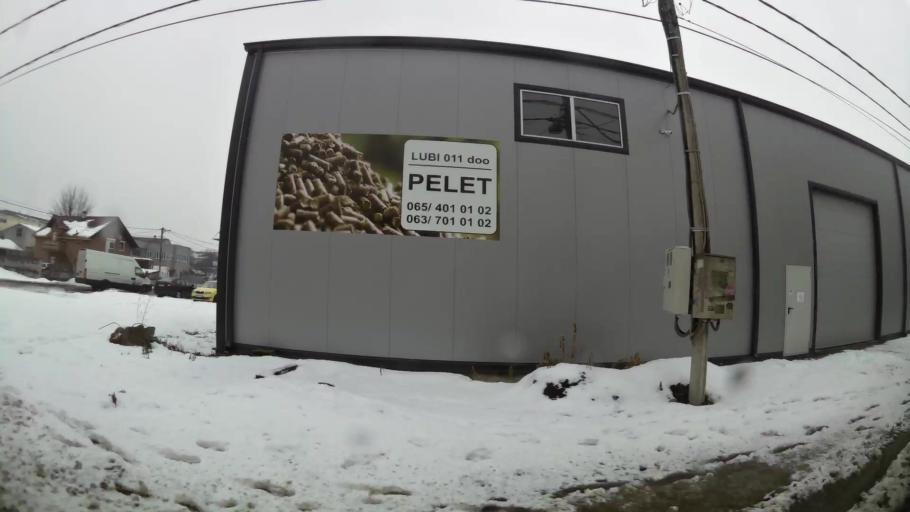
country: RS
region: Central Serbia
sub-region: Belgrade
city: Zemun
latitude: 44.8538
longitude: 20.3457
